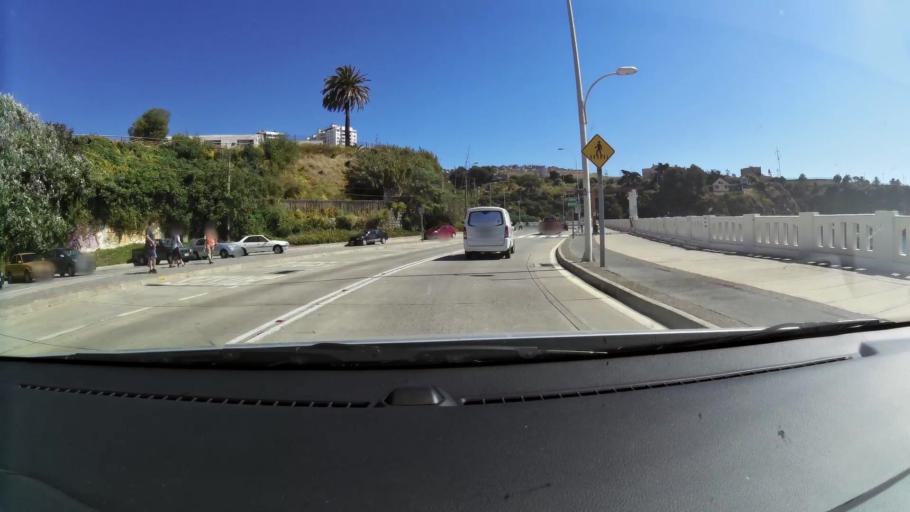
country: CL
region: Valparaiso
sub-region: Provincia de Valparaiso
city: Valparaiso
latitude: -33.0208
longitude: -71.6433
